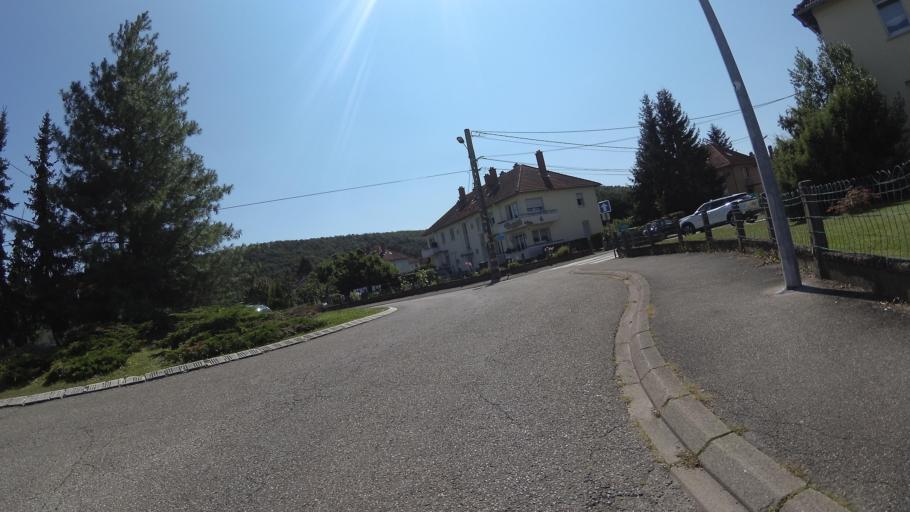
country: FR
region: Lorraine
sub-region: Departement de la Moselle
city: Stiring-Wendel
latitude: 49.2049
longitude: 6.9471
